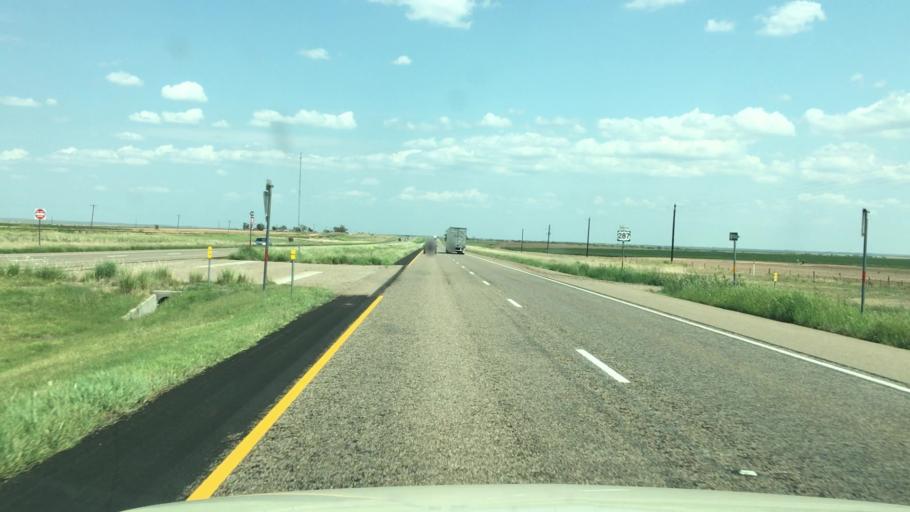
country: US
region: Texas
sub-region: Armstrong County
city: Claude
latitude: 35.0331
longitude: -101.1606
